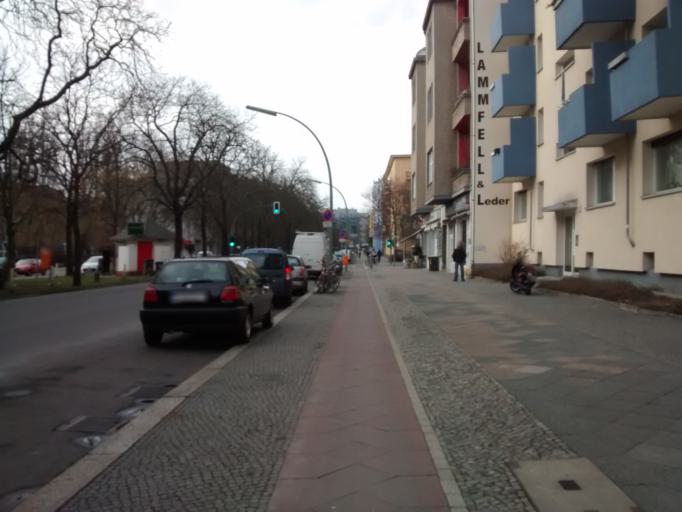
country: DE
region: Berlin
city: Moabit
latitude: 52.5211
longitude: 13.3347
